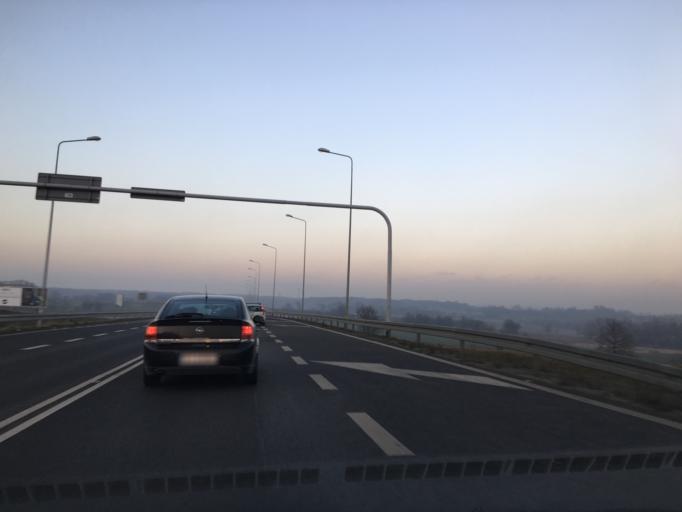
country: PL
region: Silesian Voivodeship
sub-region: Powiat tarnogorski
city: Radzionkow
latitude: 50.3573
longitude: 18.8681
